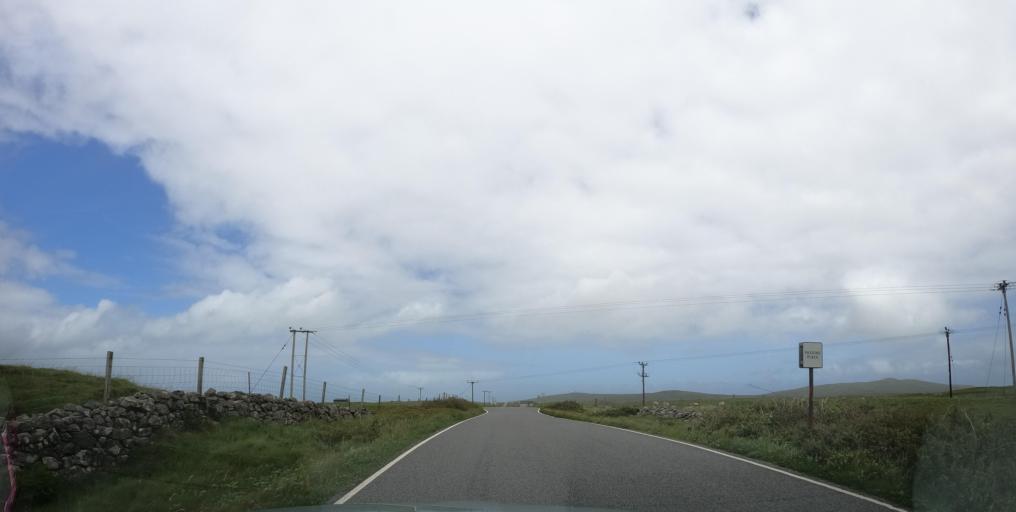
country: GB
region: Scotland
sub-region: Eilean Siar
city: Isle of South Uist
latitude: 57.3090
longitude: -7.3708
